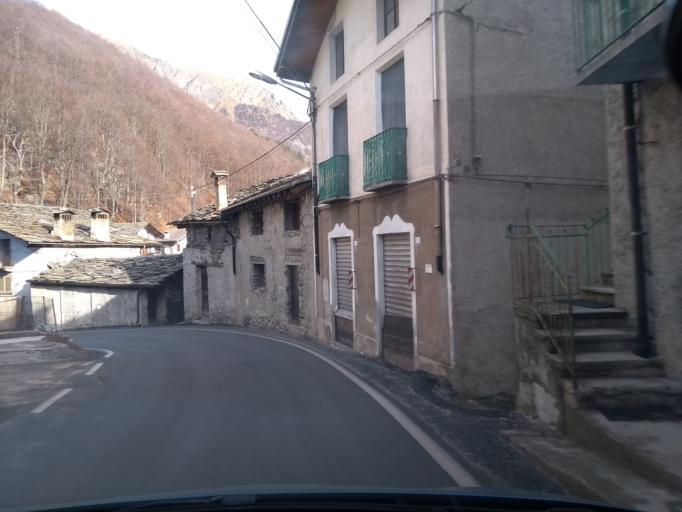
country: IT
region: Piedmont
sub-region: Provincia di Torino
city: Ala di Stura
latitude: 45.3147
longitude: 7.2912
